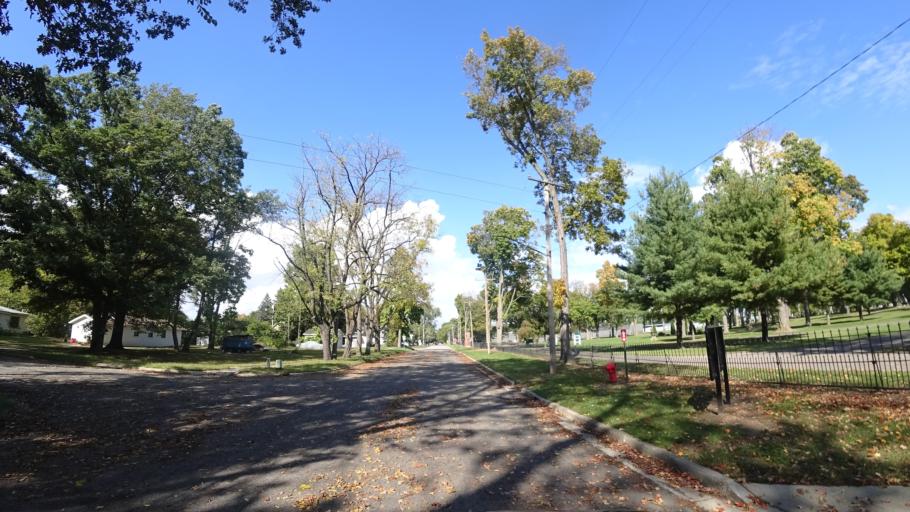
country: US
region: Michigan
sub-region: Saint Joseph County
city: Three Rivers
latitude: 41.9437
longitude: -85.6200
